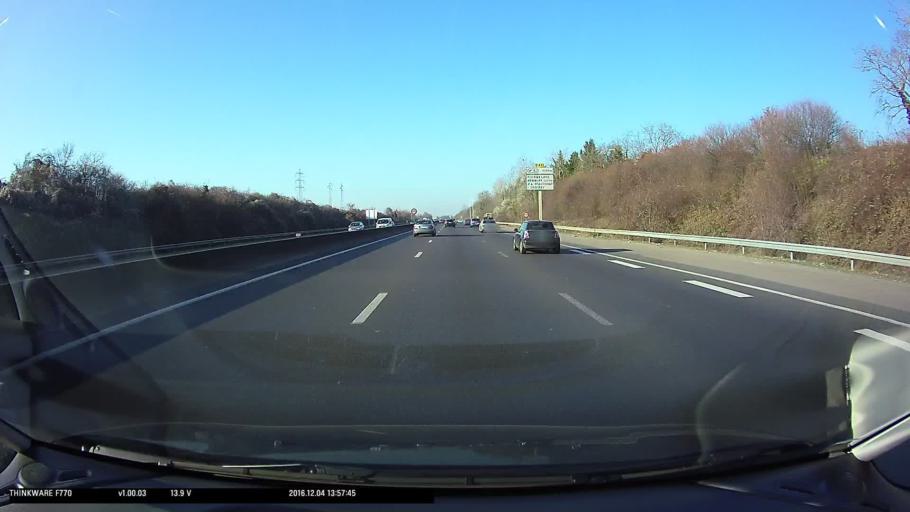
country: FR
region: Ile-de-France
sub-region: Departement du Val-d'Oise
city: Herblay
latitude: 49.0007
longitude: 2.1737
